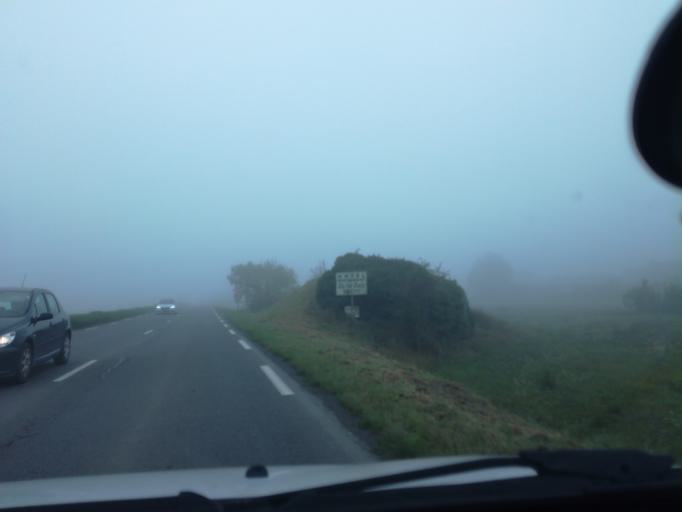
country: FR
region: Brittany
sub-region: Departement d'Ille-et-Vilaine
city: La Fresnais
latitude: 48.6262
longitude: -1.8593
